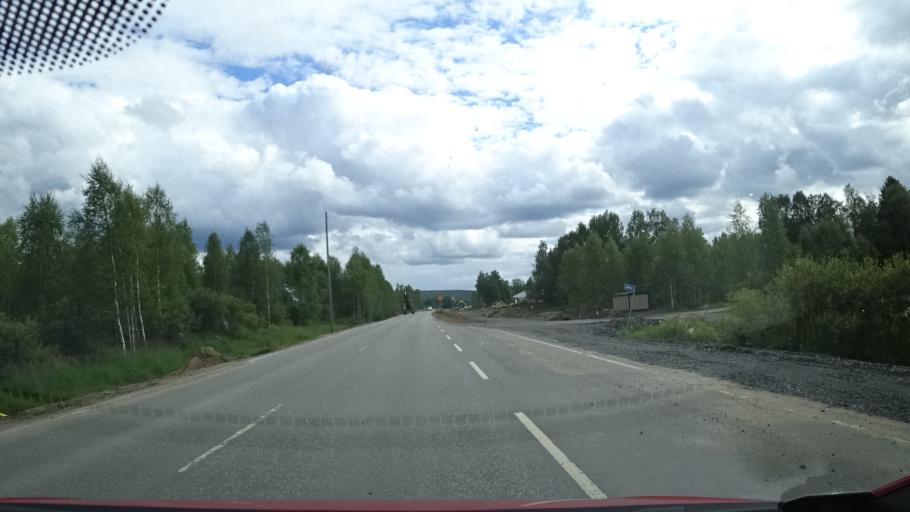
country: FI
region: Lapland
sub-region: Rovaniemi
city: Rovaniemi
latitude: 66.5292
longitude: 25.7390
